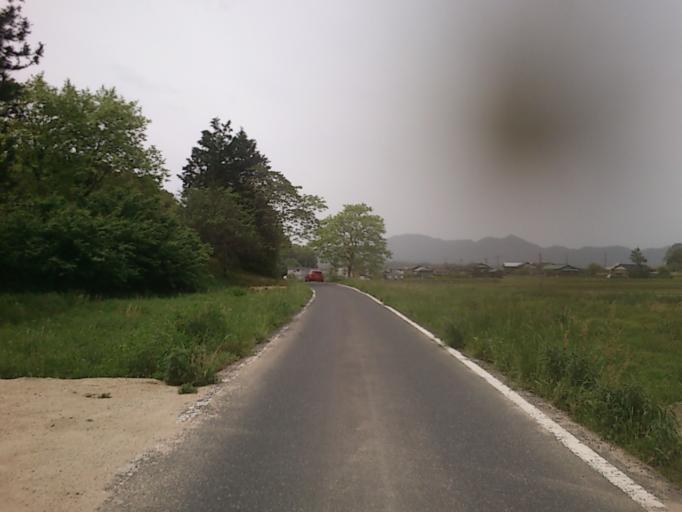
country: JP
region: Kyoto
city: Miyazu
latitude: 35.6040
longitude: 135.0983
